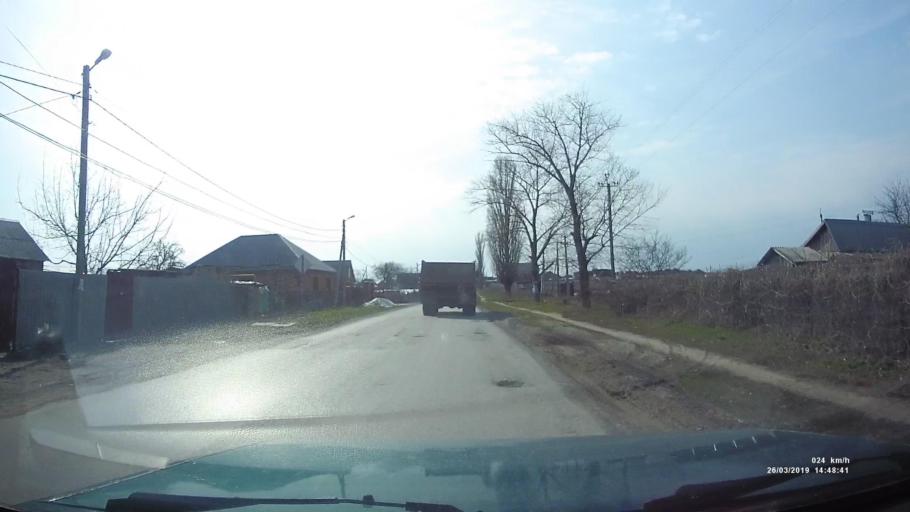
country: RU
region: Rostov
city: Novobessergenovka
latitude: 47.1907
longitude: 38.8532
